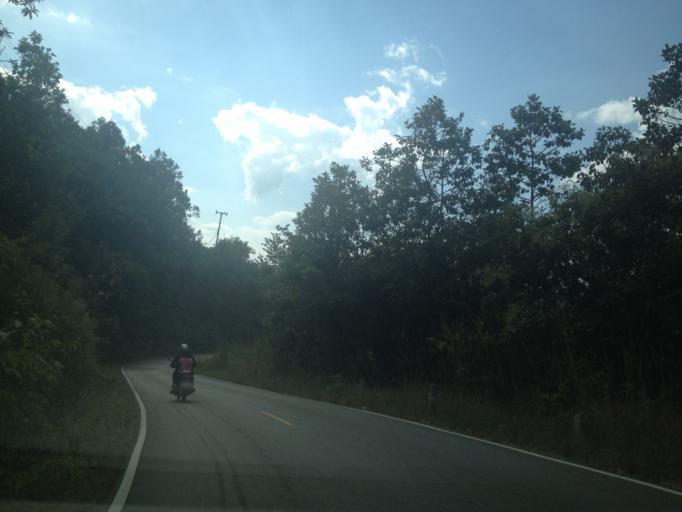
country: TH
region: Mae Hong Son
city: Ban Huai I Huak
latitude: 18.1290
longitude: 98.2195
